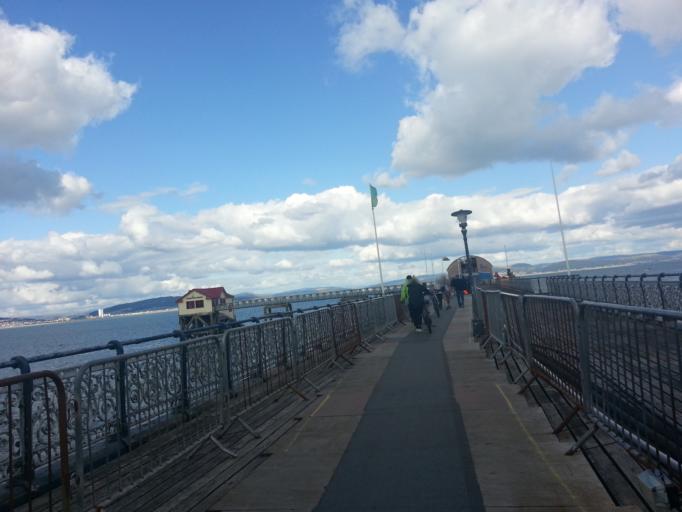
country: GB
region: Wales
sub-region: City and County of Swansea
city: Swansea
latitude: 51.5690
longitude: -3.9768
